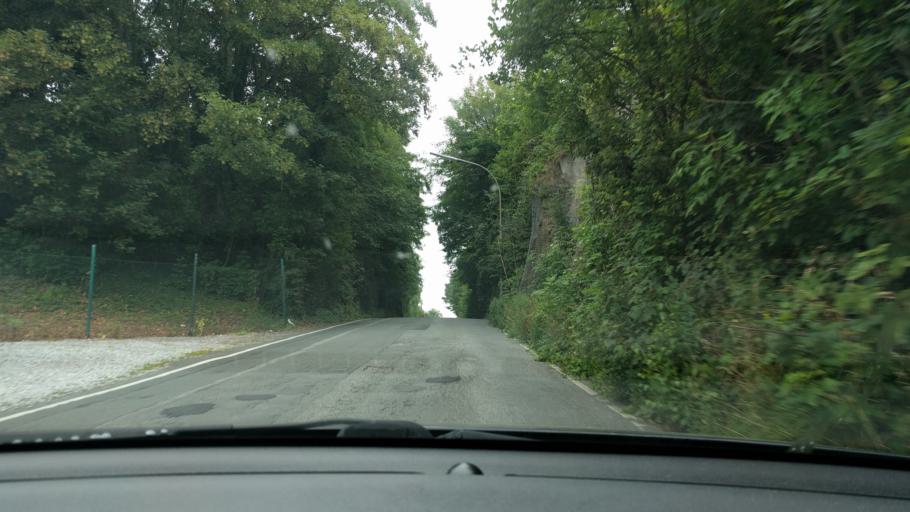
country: DE
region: North Rhine-Westphalia
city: Witten
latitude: 51.4575
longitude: 7.3734
